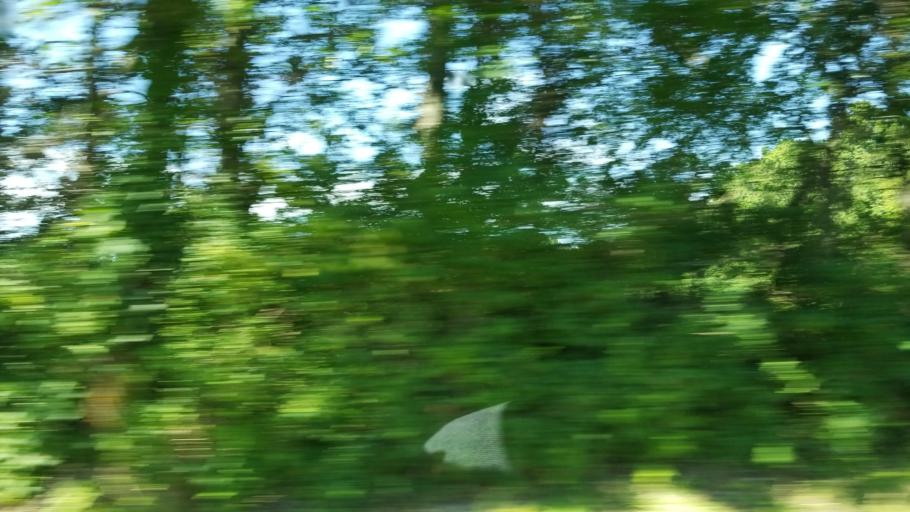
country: US
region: Illinois
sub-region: Williamson County
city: Marion
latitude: 37.7445
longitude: -88.8884
